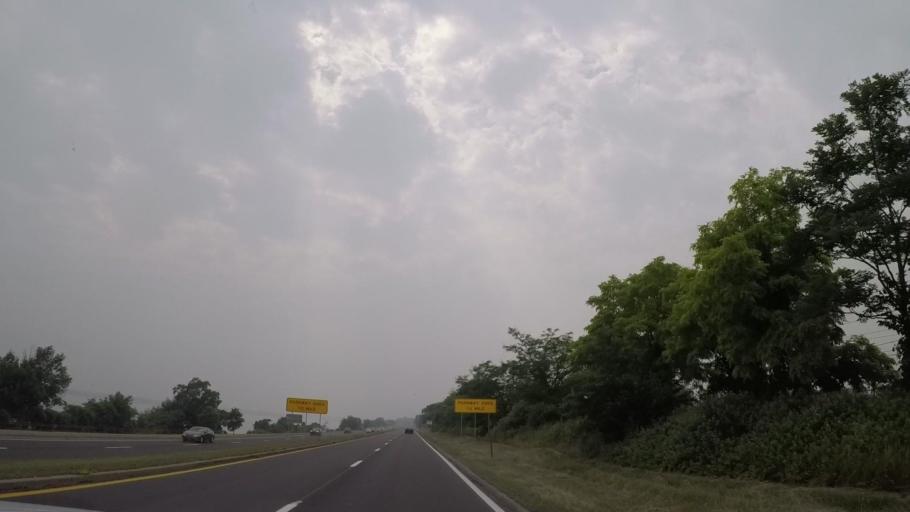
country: US
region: New York
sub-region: Niagara County
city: Niagara Falls
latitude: 43.0787
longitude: -79.0222
